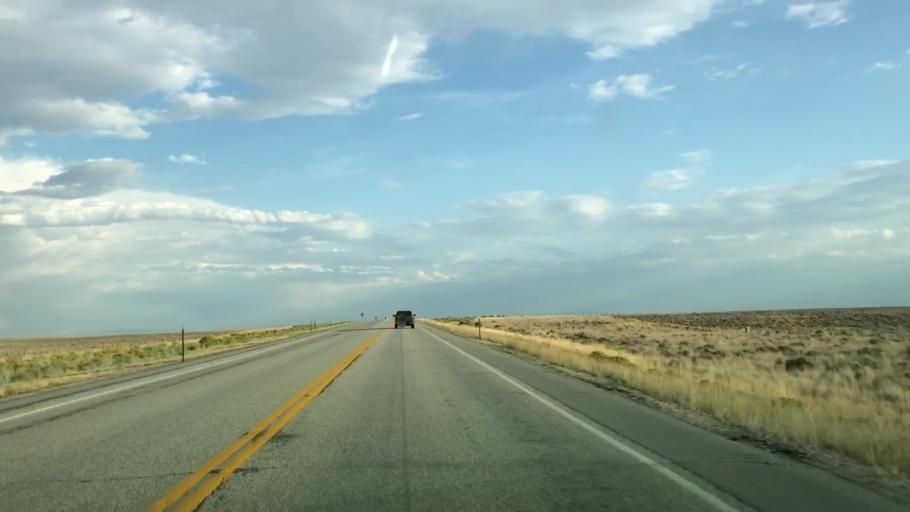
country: US
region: Wyoming
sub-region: Sublette County
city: Marbleton
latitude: 42.3216
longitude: -109.5094
